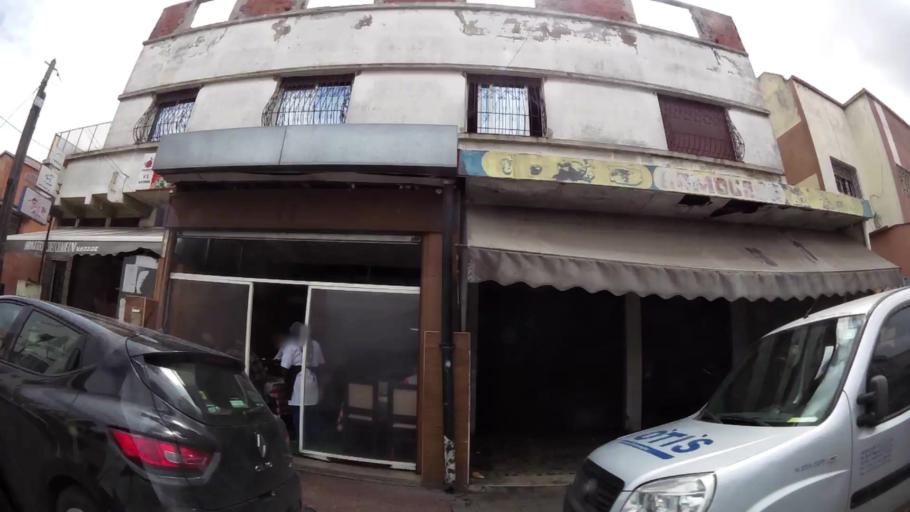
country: MA
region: Grand Casablanca
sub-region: Mediouna
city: Tit Mellil
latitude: 33.6068
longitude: -7.5385
